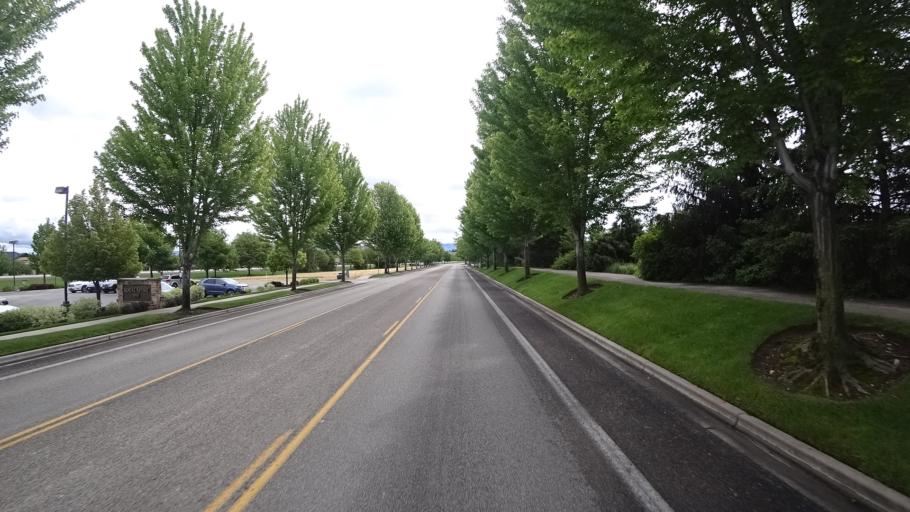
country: US
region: Idaho
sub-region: Ada County
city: Eagle
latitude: 43.6885
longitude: -116.3415
